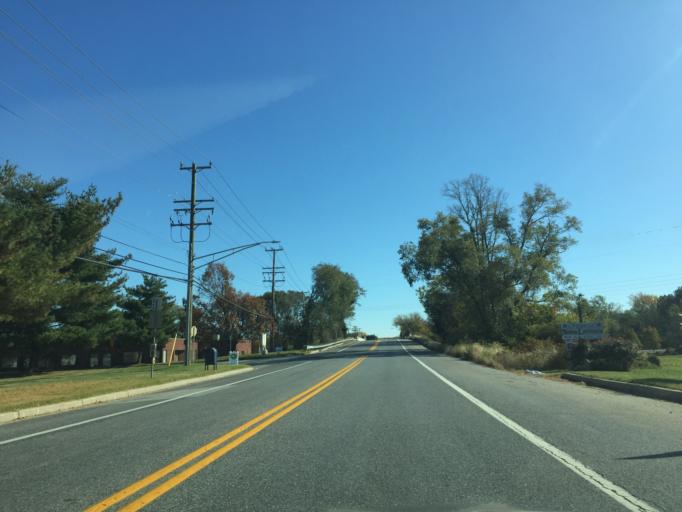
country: US
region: Maryland
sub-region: Anne Arundel County
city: Linthicum
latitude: 39.2237
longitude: -76.6551
